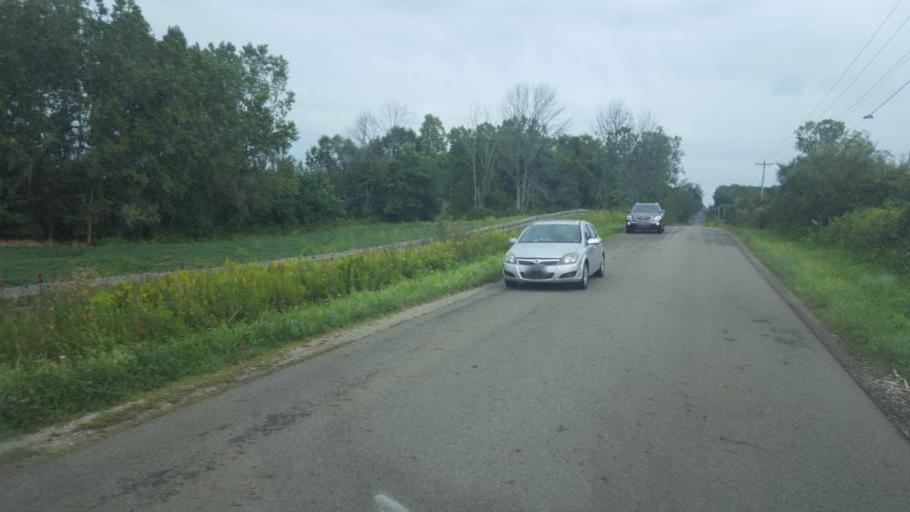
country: US
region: Ohio
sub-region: Morrow County
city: Mount Gilead
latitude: 40.5601
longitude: -82.7336
